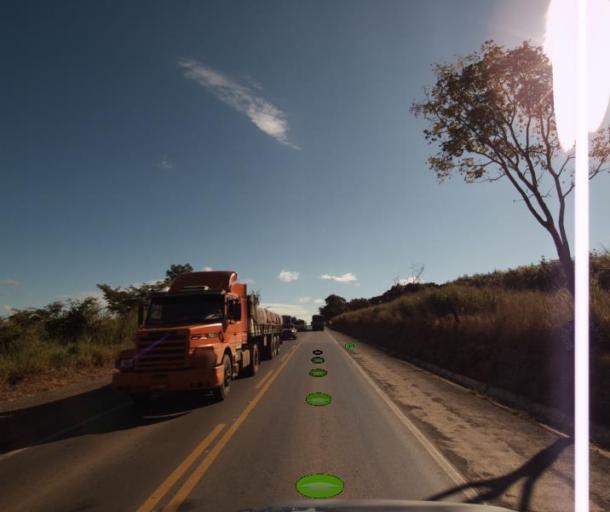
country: BR
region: Goias
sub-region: Uruacu
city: Uruacu
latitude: -14.6390
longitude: -49.1789
